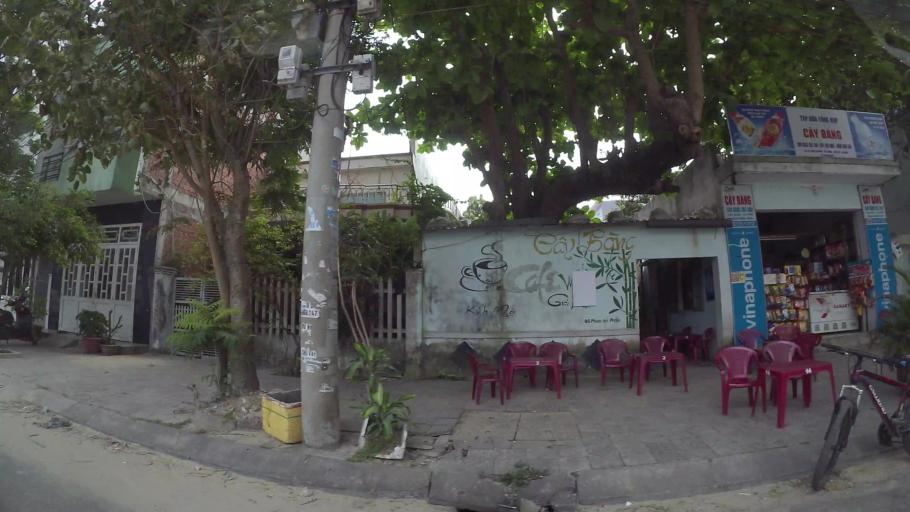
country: VN
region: Da Nang
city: Da Nang
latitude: 16.0955
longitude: 108.2456
